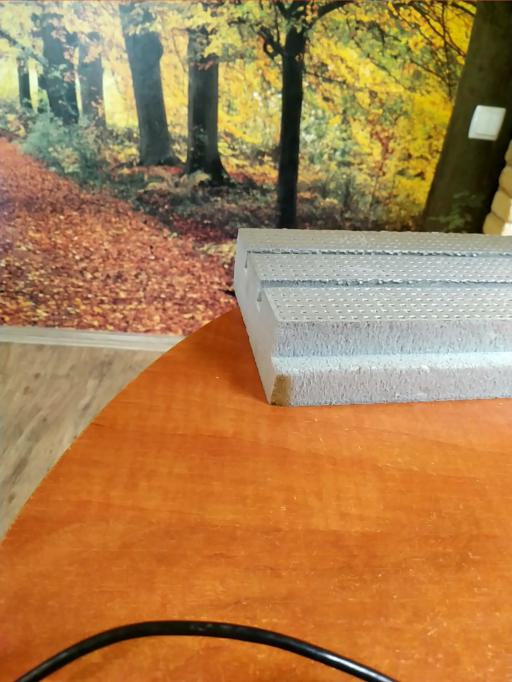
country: RU
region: Vologda
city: Babayevo
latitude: 59.1151
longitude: 36.1641
